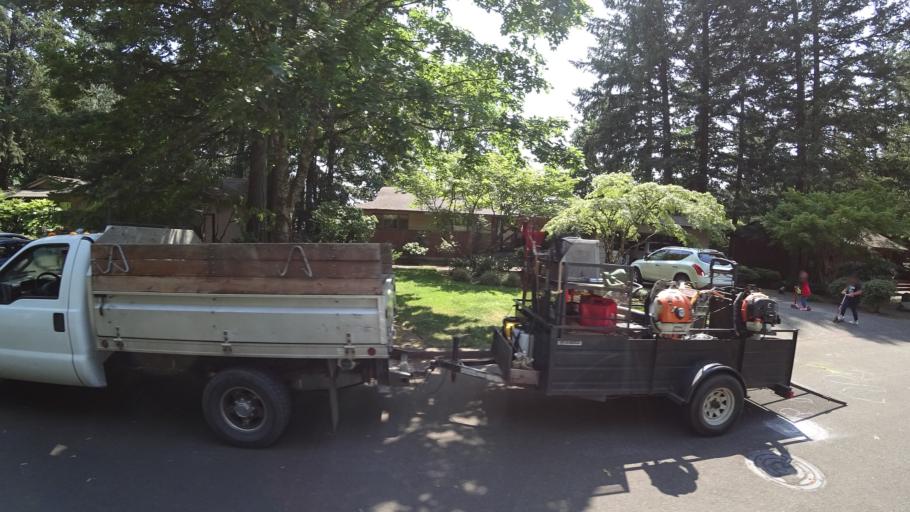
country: US
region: Oregon
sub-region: Clackamas County
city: Happy Valley
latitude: 45.4454
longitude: -122.5604
